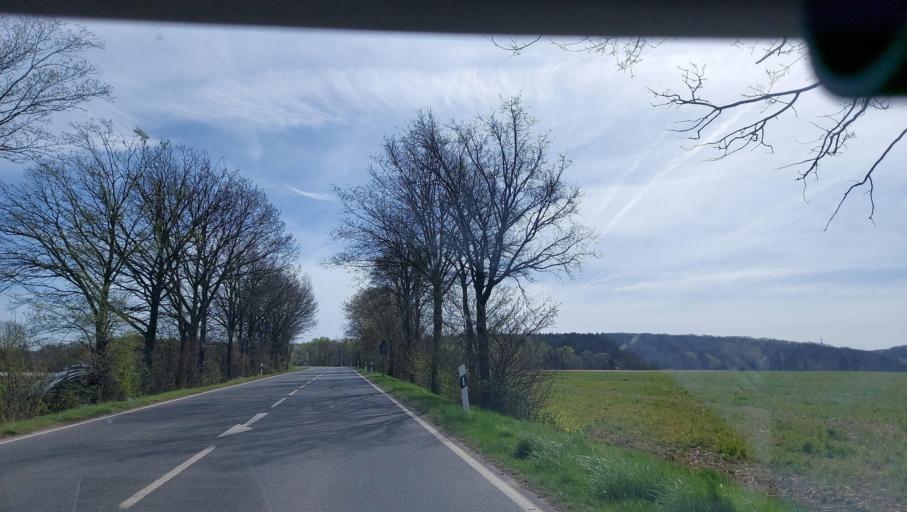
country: DE
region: North Rhine-Westphalia
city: Zulpich
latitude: 50.6545
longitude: 6.7003
